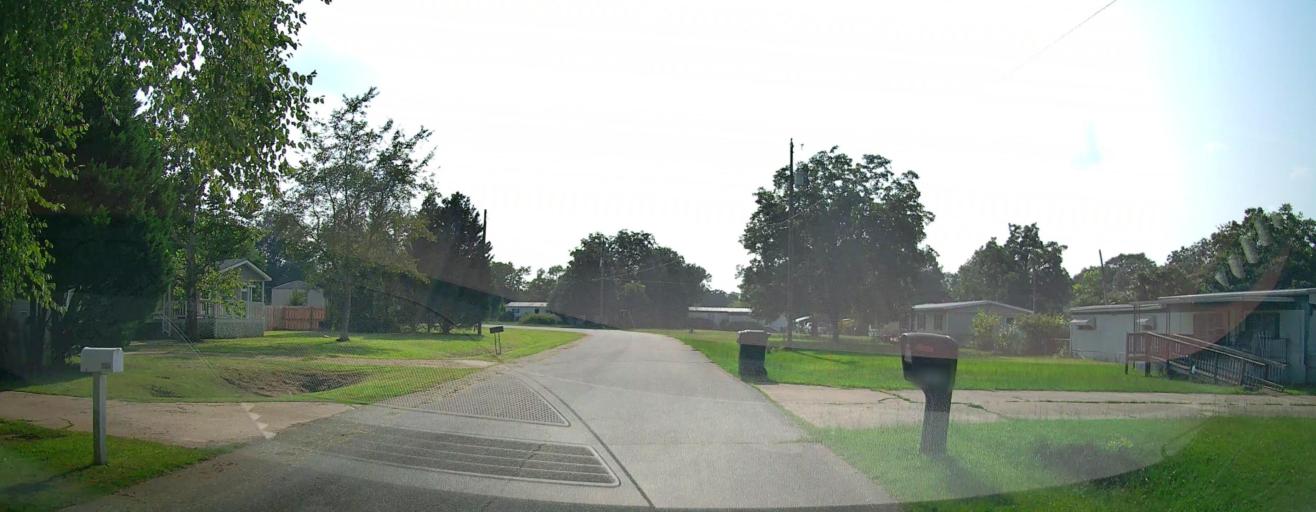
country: US
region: Georgia
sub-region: Houston County
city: Centerville
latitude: 32.6472
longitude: -83.6847
